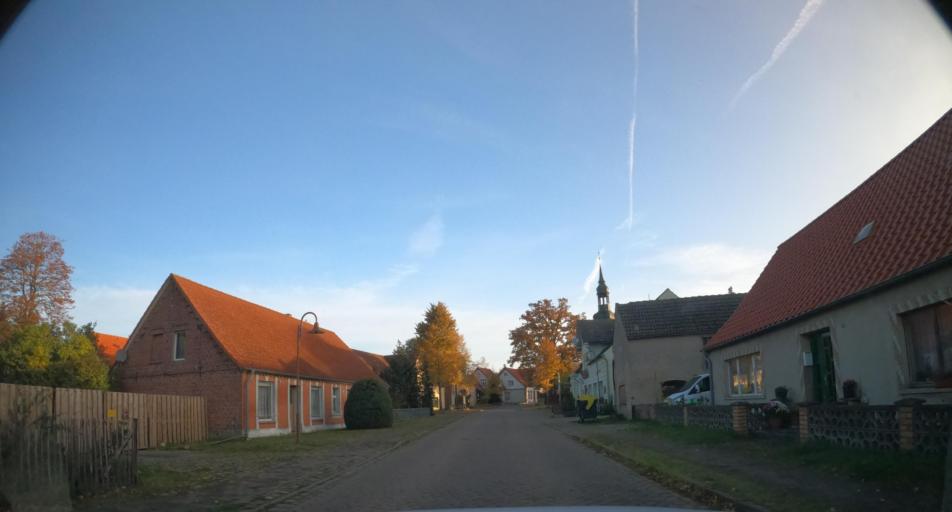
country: DE
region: Mecklenburg-Vorpommern
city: Ahlbeck
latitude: 53.6700
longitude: 14.1860
